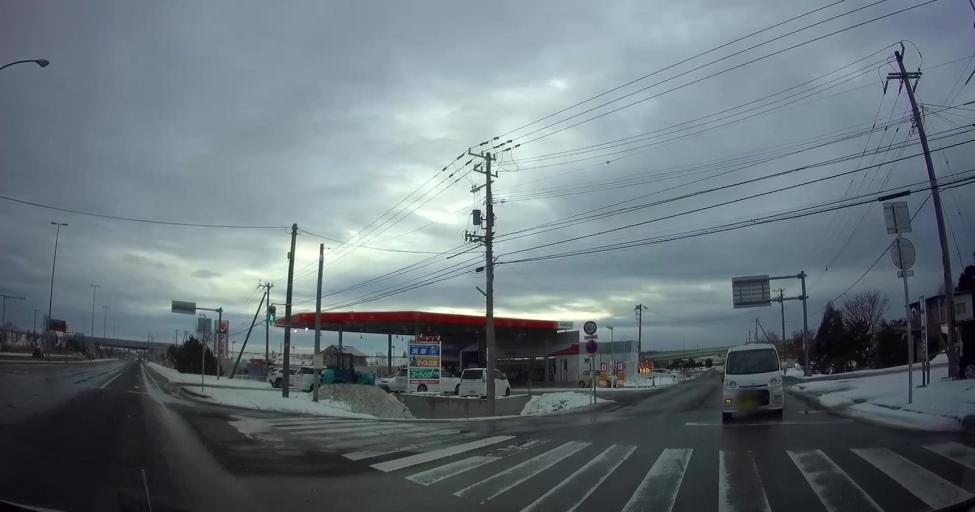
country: JP
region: Hokkaido
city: Nanae
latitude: 41.8369
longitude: 140.6919
